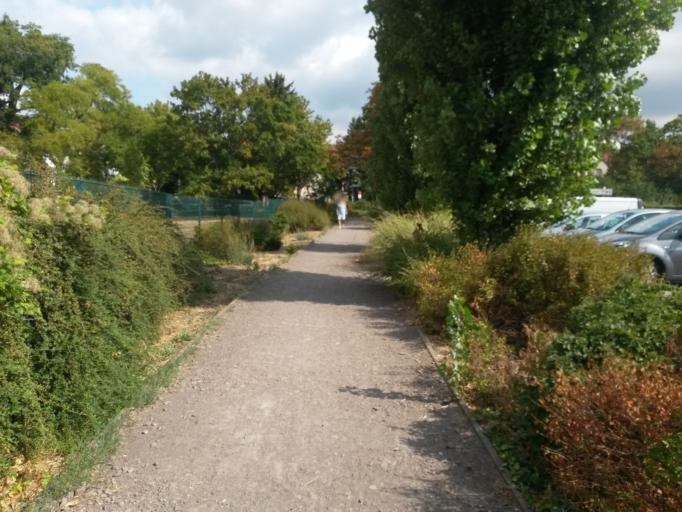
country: DE
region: Saxony-Anhalt
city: Wittenburg
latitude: 51.8641
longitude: 12.6466
